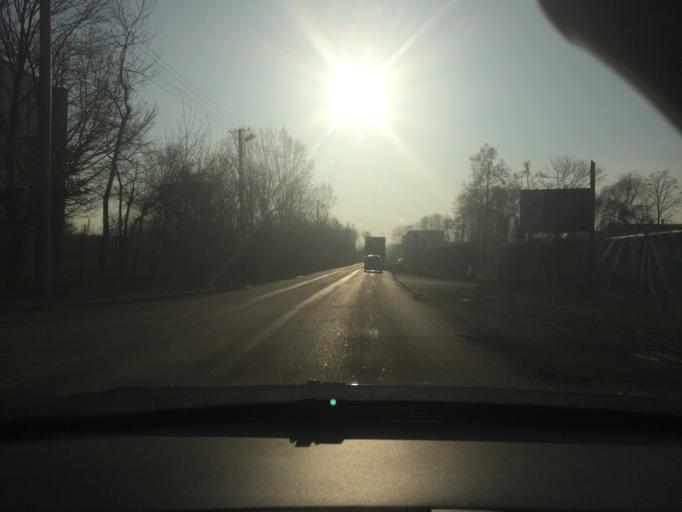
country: PL
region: Lesser Poland Voivodeship
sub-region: Powiat wielicki
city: Czarnochowice
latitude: 50.0282
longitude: 20.0393
